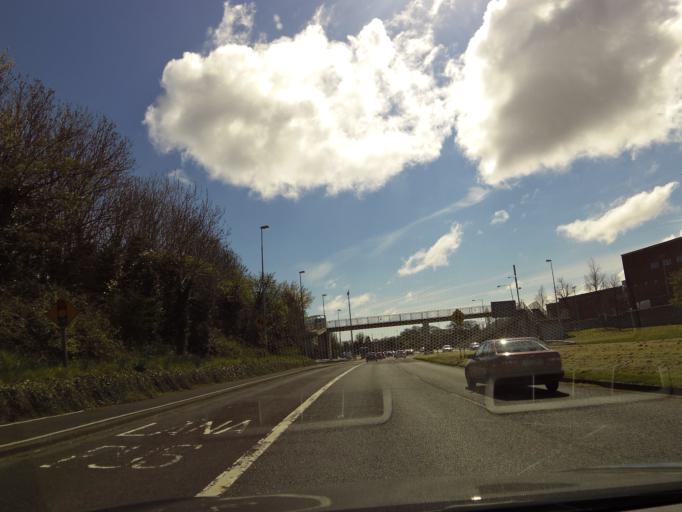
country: IE
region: Leinster
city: Cabinteely
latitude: 53.2677
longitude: -6.1598
